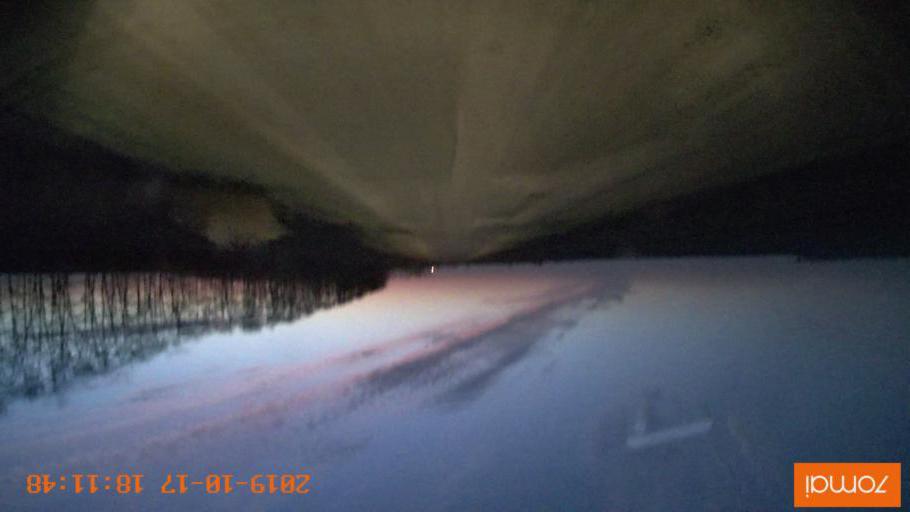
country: RU
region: Tula
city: Kurkino
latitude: 53.4122
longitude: 38.6176
